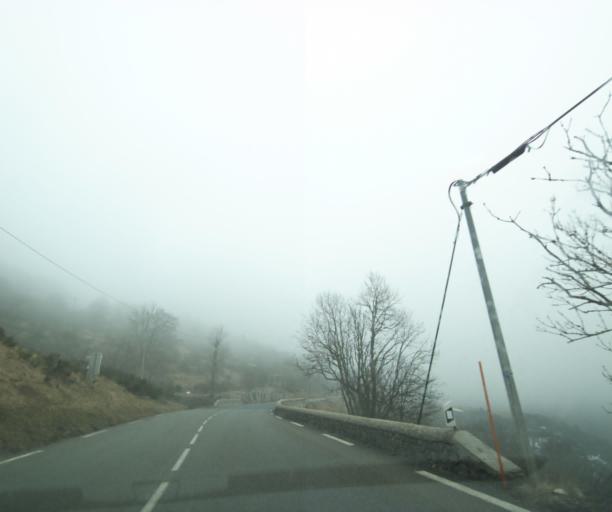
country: FR
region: Languedoc-Roussillon
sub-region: Departement de la Lozere
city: Langogne
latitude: 44.6963
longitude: 4.0265
